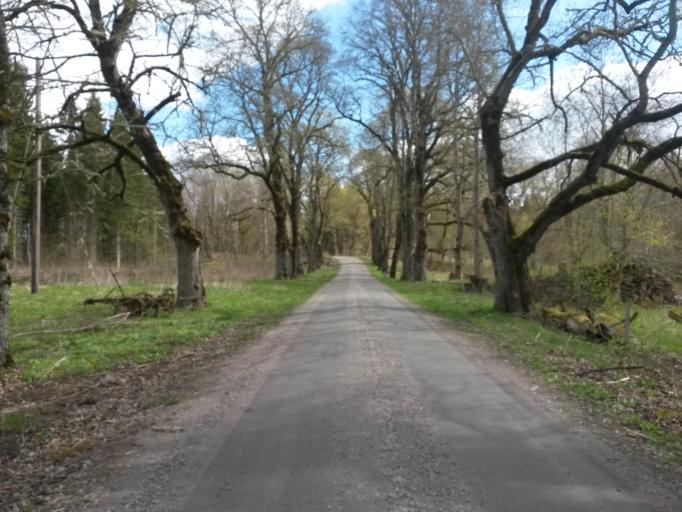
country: SE
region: Vaestra Goetaland
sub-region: Falkopings Kommun
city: Floby
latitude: 58.1641
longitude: 13.2821
